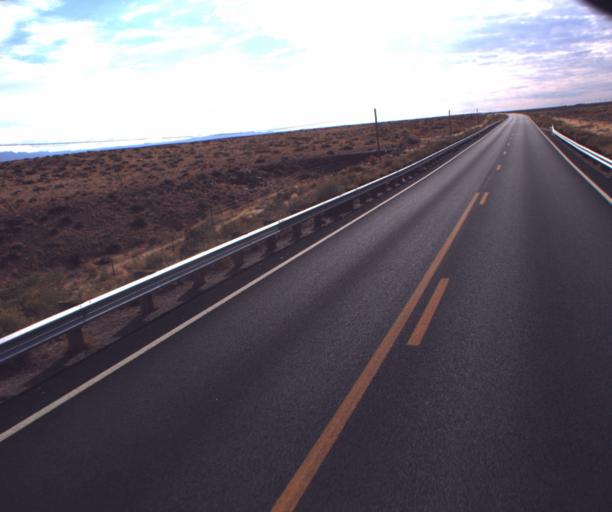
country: US
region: Arizona
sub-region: Apache County
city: Many Farms
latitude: 36.5662
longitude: -109.5442
